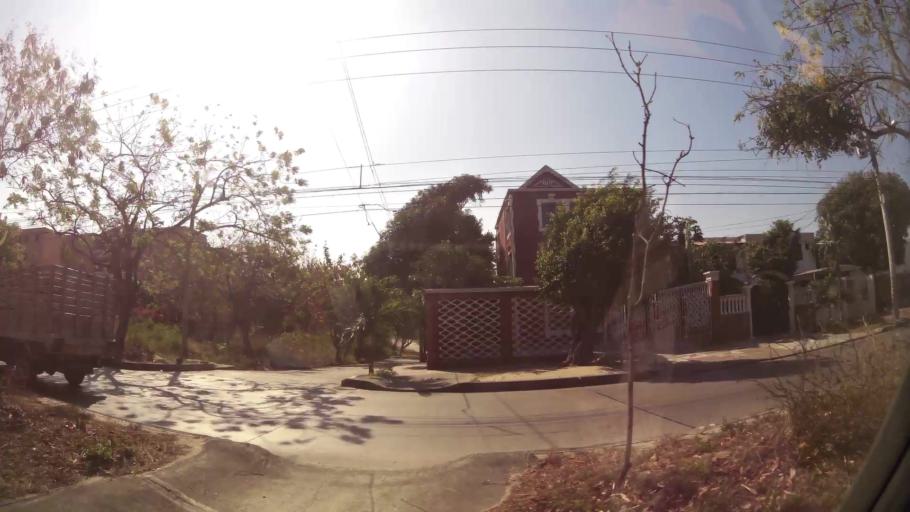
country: CO
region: Atlantico
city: Barranquilla
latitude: 10.9879
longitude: -74.8303
